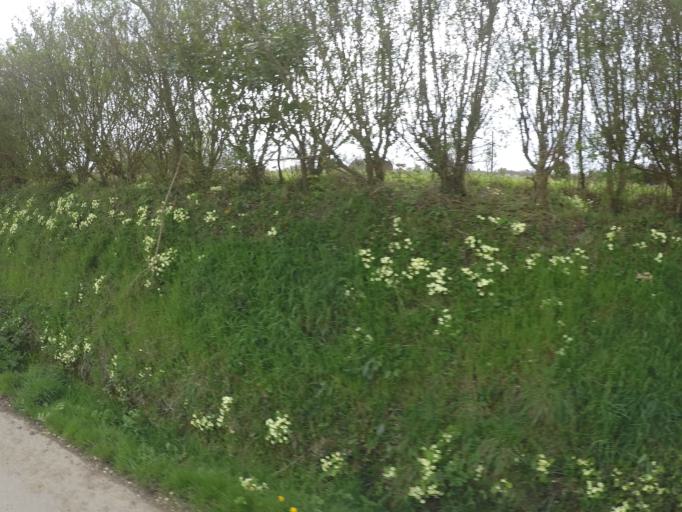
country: FR
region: Brittany
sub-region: Departement des Cotes-d'Armor
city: Plouha
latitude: 48.7109
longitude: -2.9396
